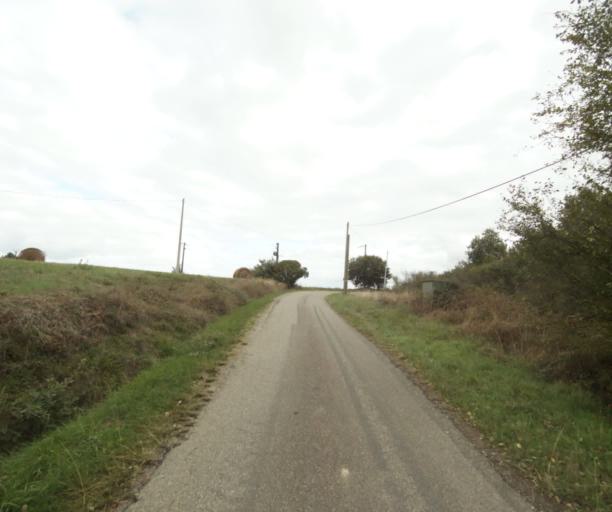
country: FR
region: Midi-Pyrenees
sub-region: Departement du Tarn-et-Garonne
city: Beaumont-de-Lomagne
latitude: 43.8876
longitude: 1.0811
